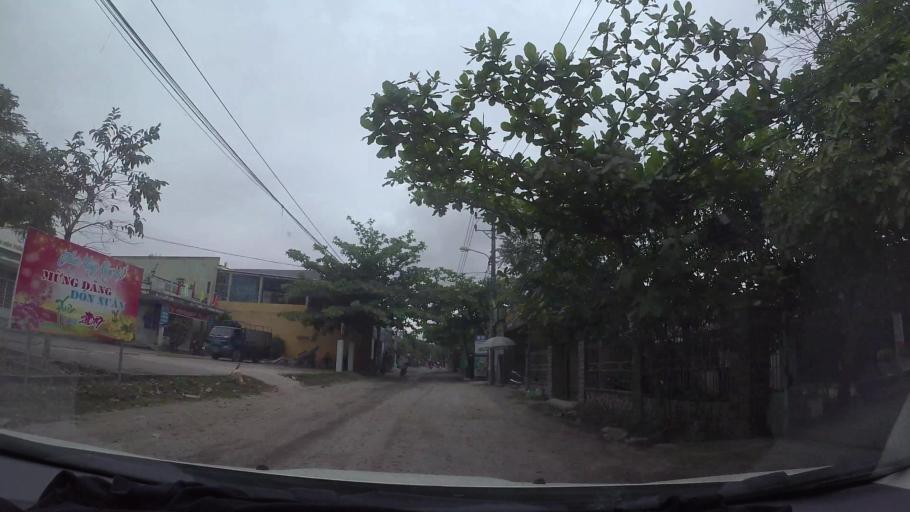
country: VN
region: Da Nang
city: Lien Chieu
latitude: 16.0772
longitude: 108.0990
